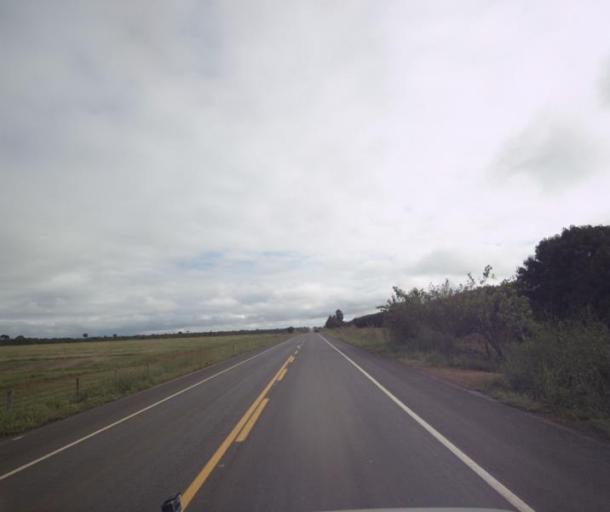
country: BR
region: Goias
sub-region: Padre Bernardo
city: Padre Bernardo
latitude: -15.3739
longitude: -48.6455
